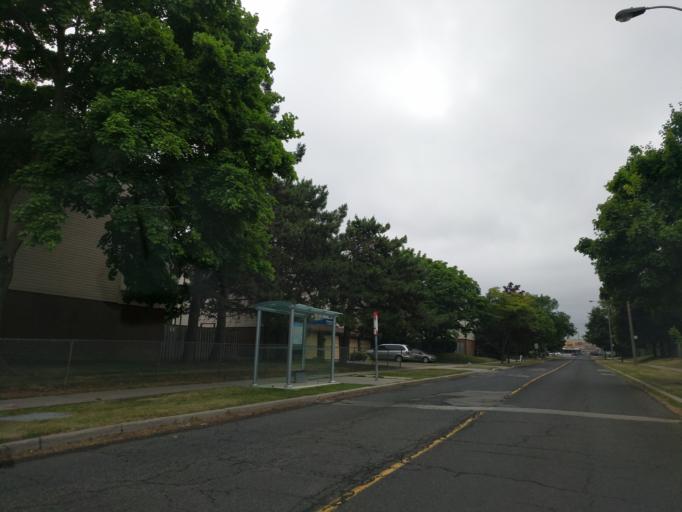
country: CA
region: Ontario
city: Willowdale
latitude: 43.8100
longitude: -79.3567
